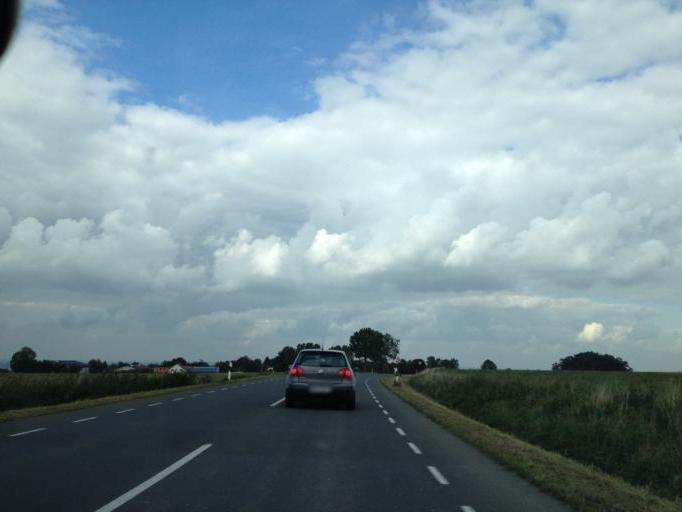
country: DE
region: North Rhine-Westphalia
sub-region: Regierungsbezirk Arnsberg
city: Soest
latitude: 51.5246
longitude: 8.0760
